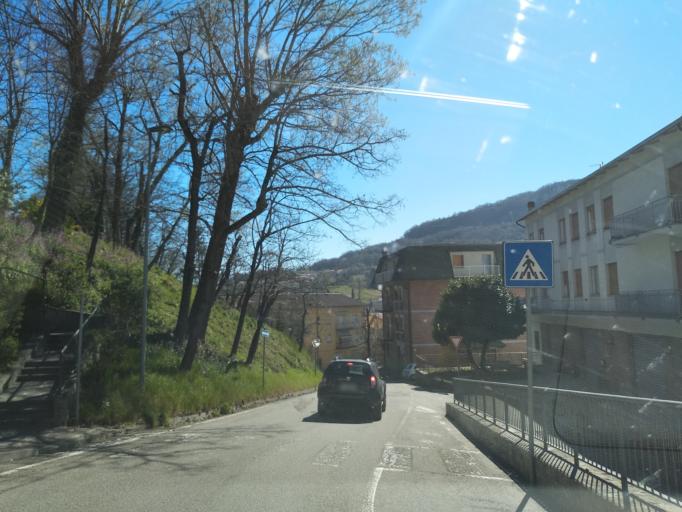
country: IT
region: Emilia-Romagna
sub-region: Provincia di Reggio Emilia
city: Castelnovo ne'Monti
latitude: 44.4332
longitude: 10.4006
